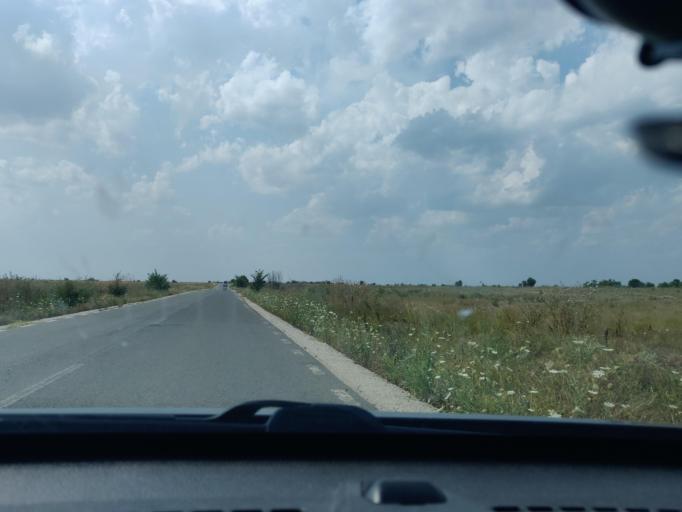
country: RO
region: Teleorman
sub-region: Comuna Gratia
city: Draghinesti
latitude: 44.4445
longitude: 25.4340
